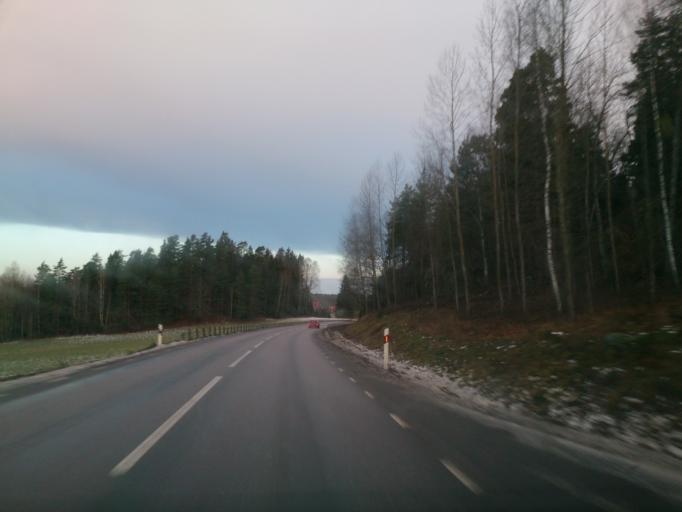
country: SE
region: OEstergoetland
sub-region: Atvidabergs Kommun
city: Atvidaberg
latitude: 58.2840
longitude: 15.9001
